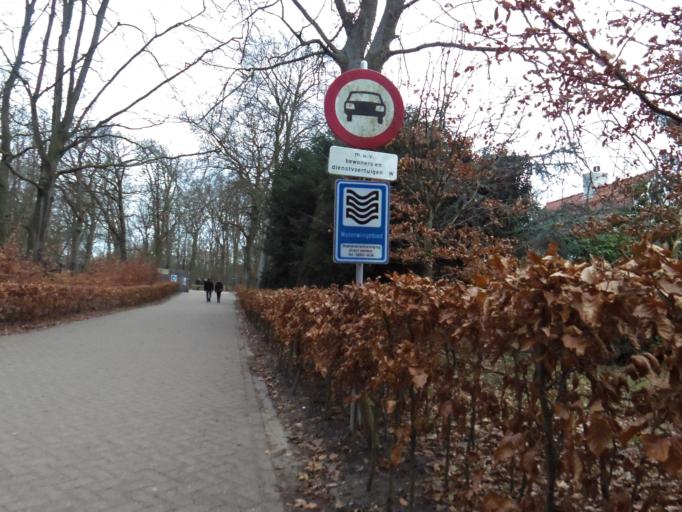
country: NL
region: North Holland
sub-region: Gemeente Bloemendaal
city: Bennebroek
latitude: 52.3311
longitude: 4.5654
